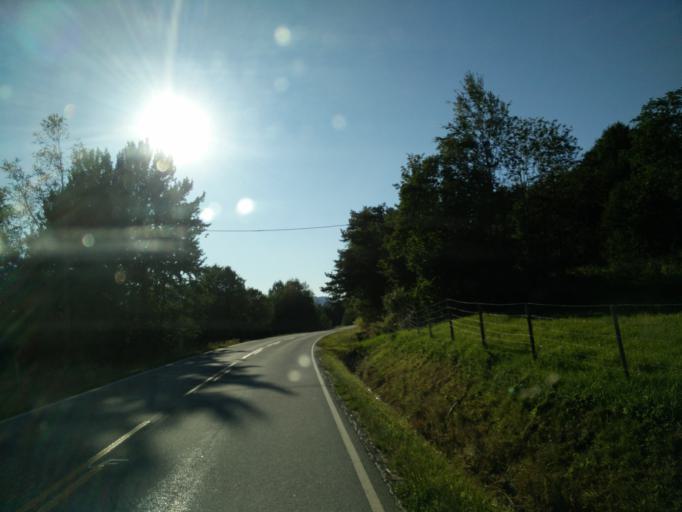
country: NO
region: More og Romsdal
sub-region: Halsa
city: Liaboen
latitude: 63.0840
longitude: 8.4059
